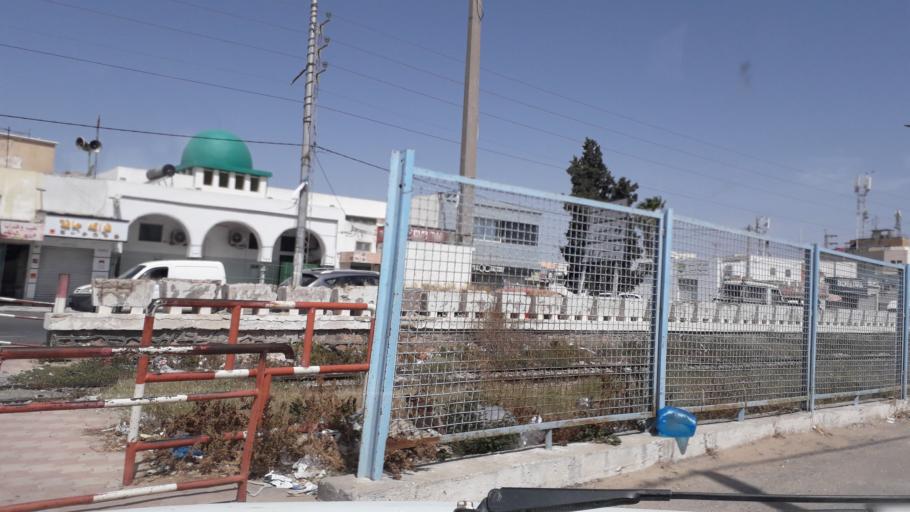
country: TN
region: Safaqis
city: Al Qarmadah
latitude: 34.8015
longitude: 10.7614
